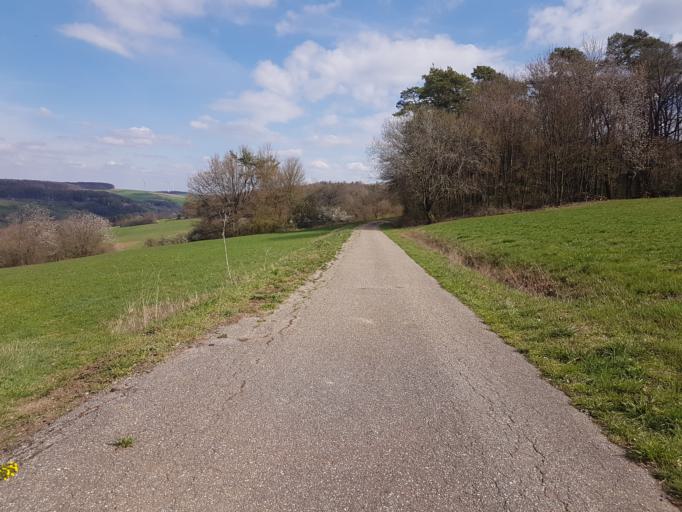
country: DE
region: Baden-Wuerttemberg
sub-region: Regierungsbezirk Stuttgart
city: Niedernhall
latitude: 49.3390
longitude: 9.6201
